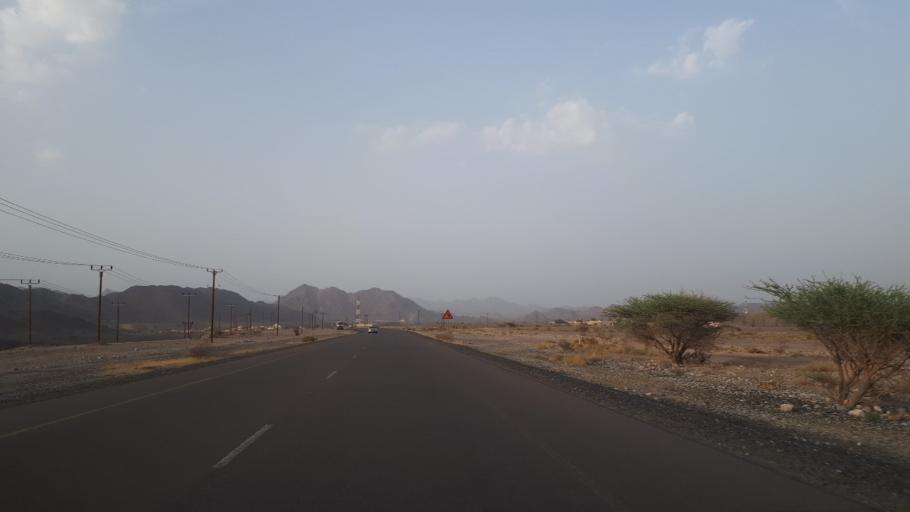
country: OM
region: Al Batinah
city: Rustaq
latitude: 23.3903
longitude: 57.2314
